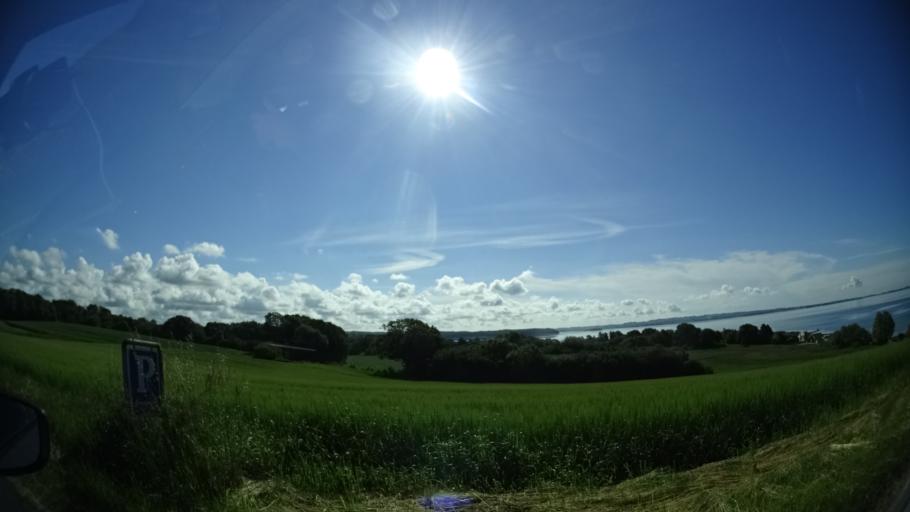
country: DK
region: Central Jutland
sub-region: Syddjurs Kommune
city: Ronde
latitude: 56.2944
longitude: 10.4099
